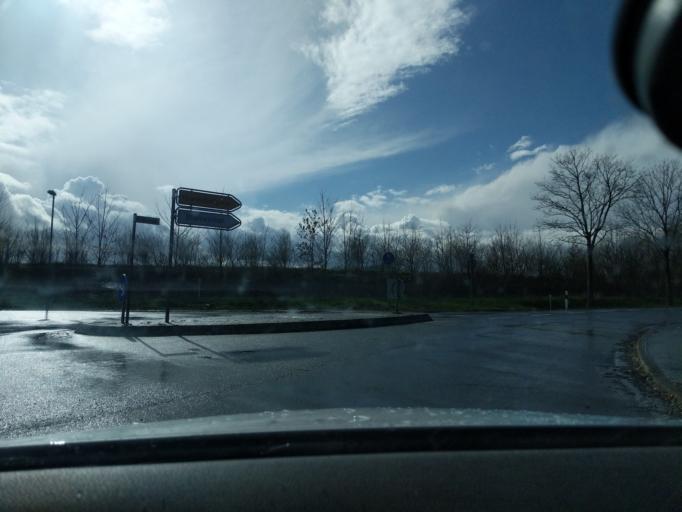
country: DE
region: Lower Saxony
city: Burweg
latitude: 53.6202
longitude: 9.2555
